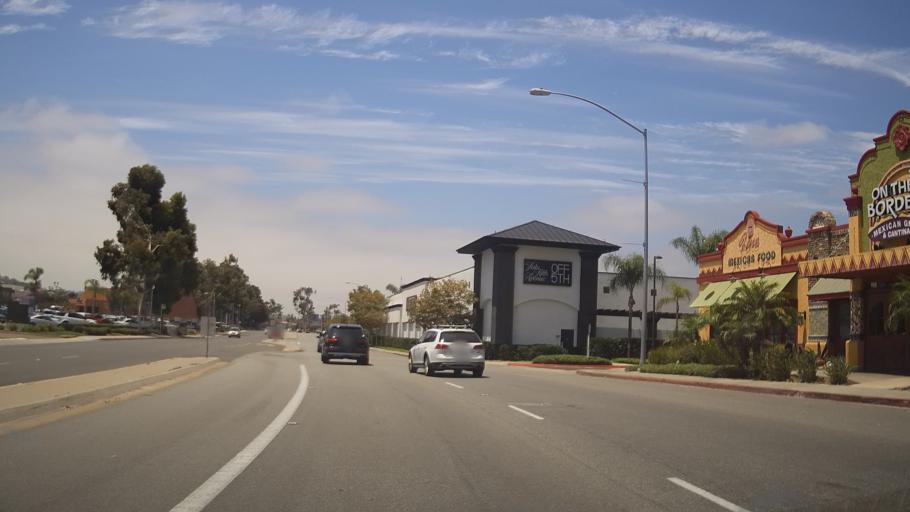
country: US
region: California
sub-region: San Diego County
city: San Diego
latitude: 32.7708
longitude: -117.1463
